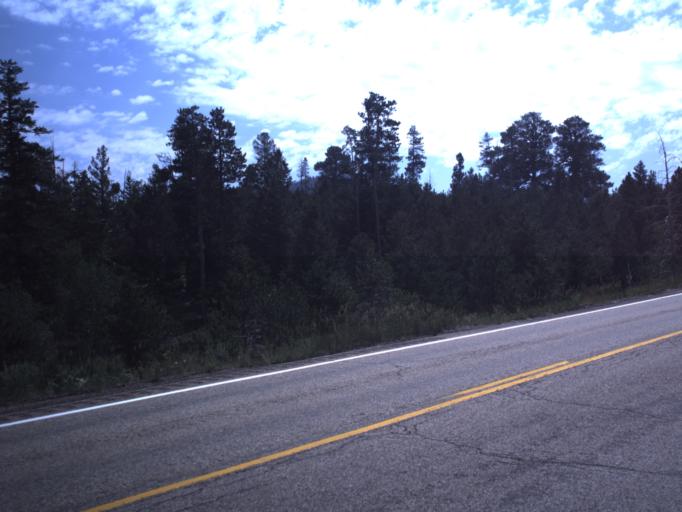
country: US
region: Utah
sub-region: Daggett County
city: Manila
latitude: 40.8557
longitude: -109.4634
